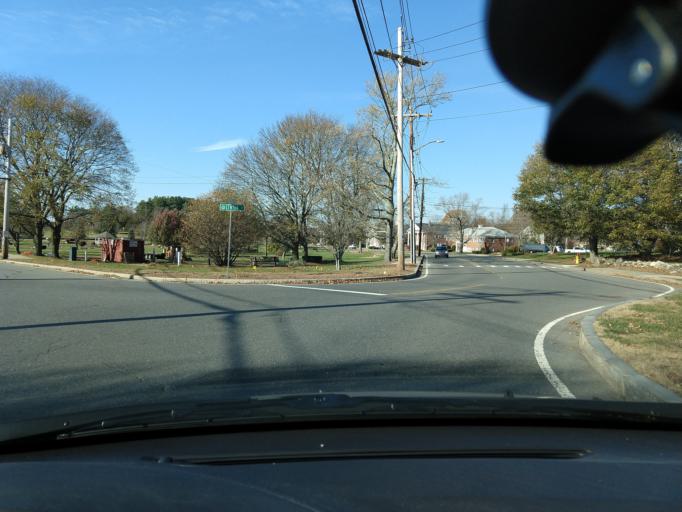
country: US
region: Massachusetts
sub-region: Middlesex County
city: Burlington
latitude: 42.5045
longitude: -71.1927
